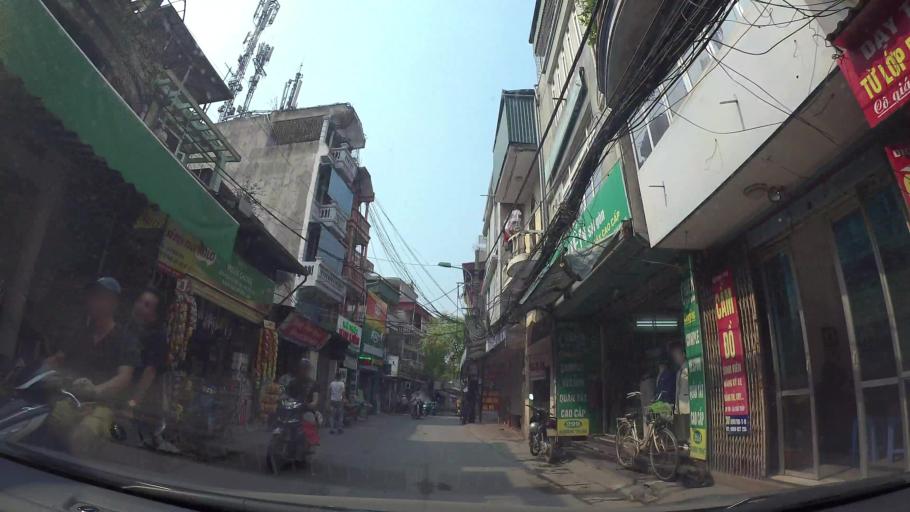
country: VN
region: Ha Noi
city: Thanh Xuan
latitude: 20.9936
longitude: 105.8173
